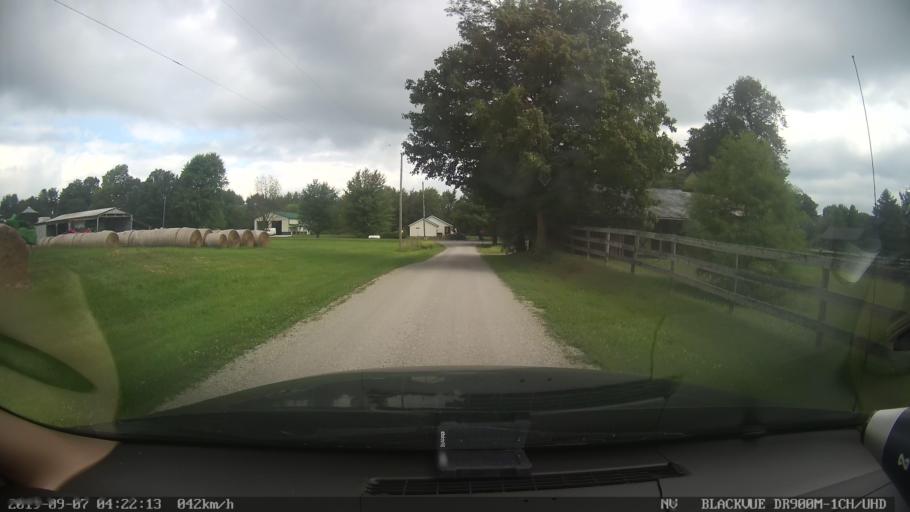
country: US
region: Ohio
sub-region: Knox County
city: Centerburg
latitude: 40.2729
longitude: -82.6717
